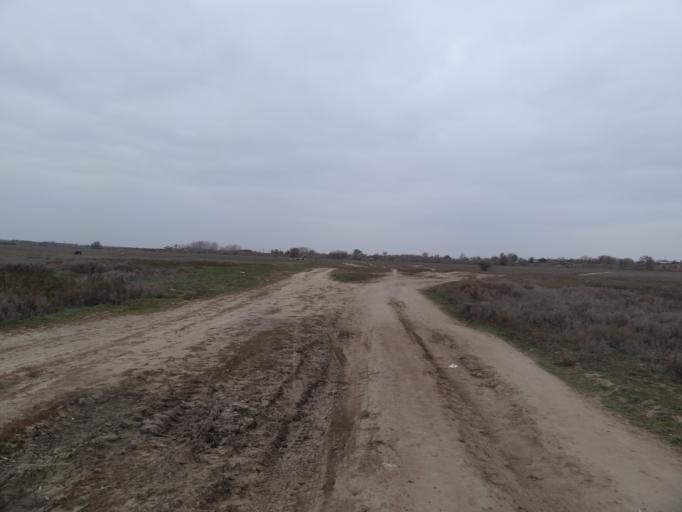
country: RU
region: Saratov
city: Sovetskoye
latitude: 51.5317
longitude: 46.6068
